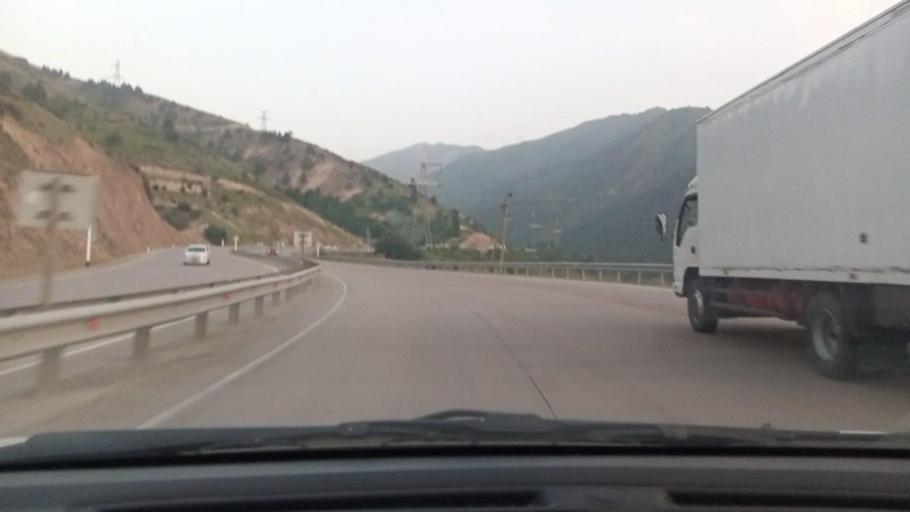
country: UZ
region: Toshkent
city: Angren
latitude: 41.1521
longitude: 70.4443
